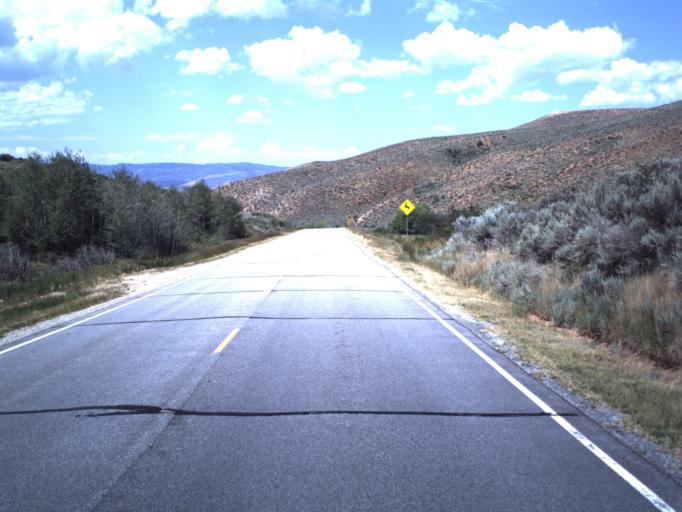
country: US
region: Utah
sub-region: Rich County
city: Randolph
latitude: 41.8124
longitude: -111.2651
